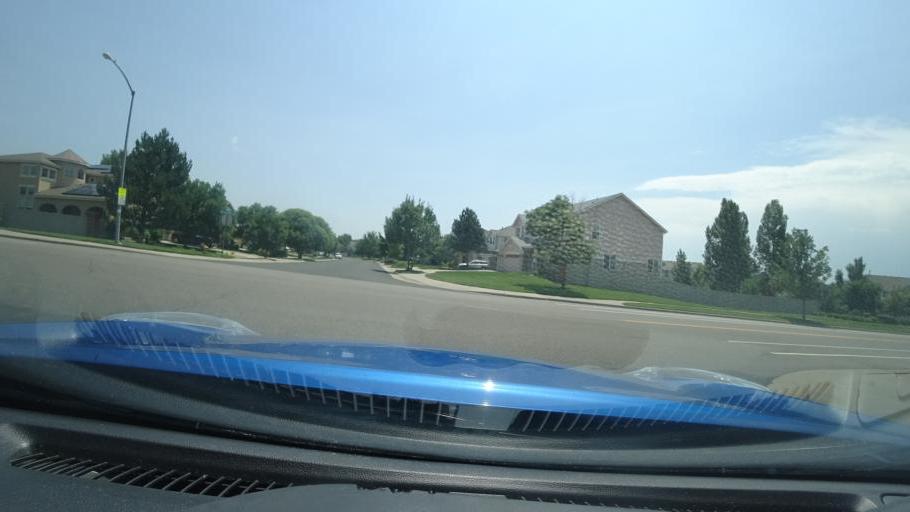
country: US
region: Colorado
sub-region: Adams County
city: Aurora
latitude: 39.6733
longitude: -104.7640
